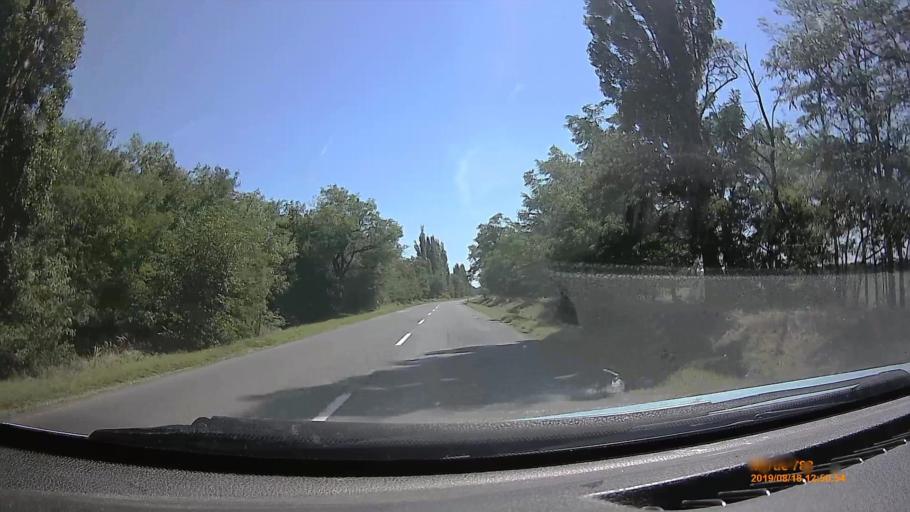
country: HU
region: Fejer
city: Aba
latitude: 47.0798
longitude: 18.5033
